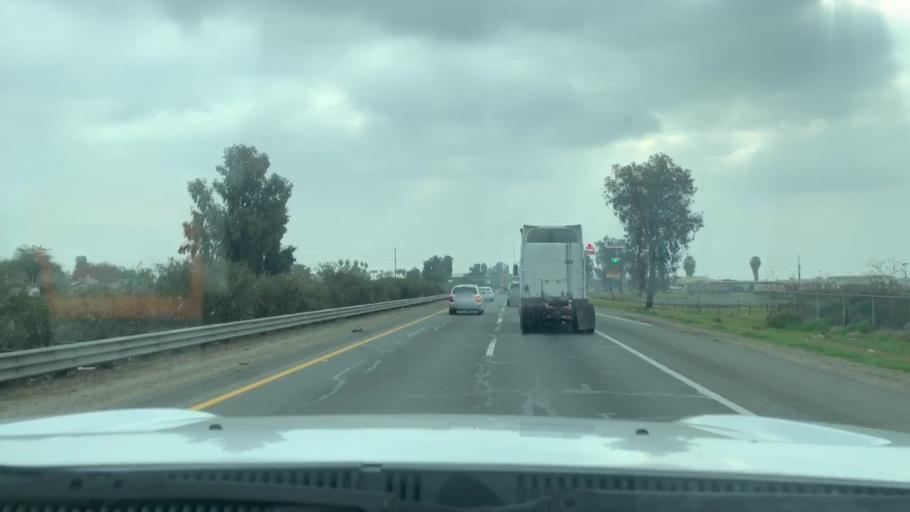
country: US
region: California
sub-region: Tulare County
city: Tulare
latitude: 36.1861
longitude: -119.3287
